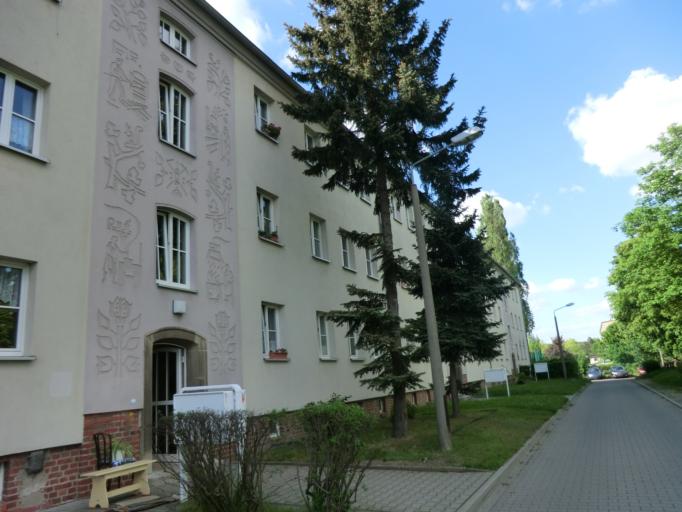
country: DE
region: Saxony
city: Goerlitz
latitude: 51.1233
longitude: 14.9797
